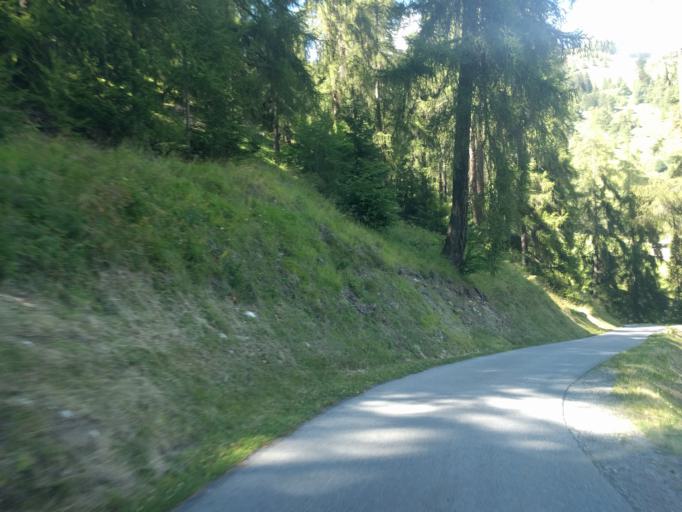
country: IT
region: Trentino-Alto Adige
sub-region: Bolzano
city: Tubre
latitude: 46.6120
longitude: 10.4224
